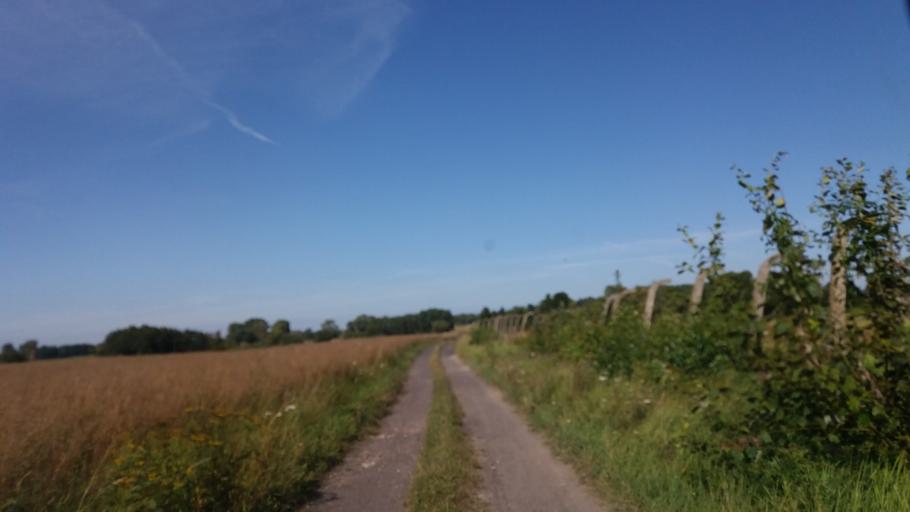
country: PL
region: West Pomeranian Voivodeship
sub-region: Powiat choszczenski
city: Choszczno
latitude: 53.1543
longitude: 15.4496
